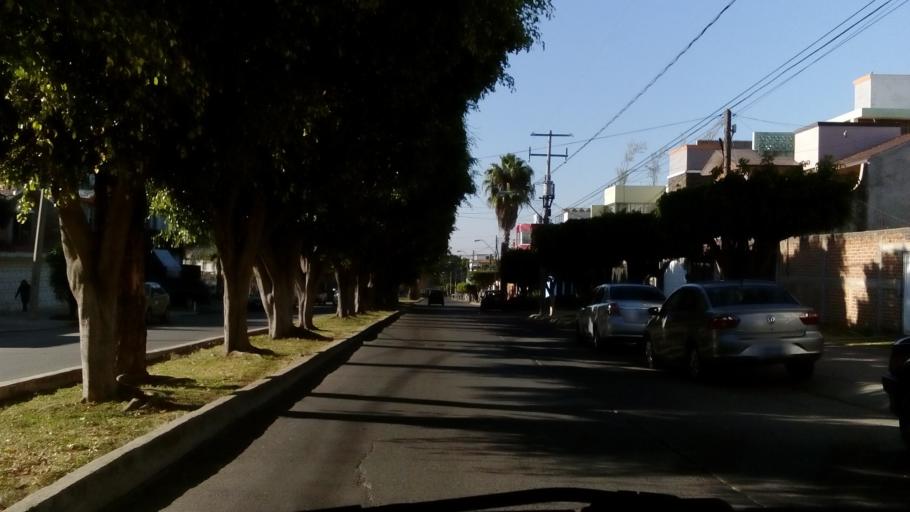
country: MX
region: Guanajuato
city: Leon
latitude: 21.1186
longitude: -101.6988
